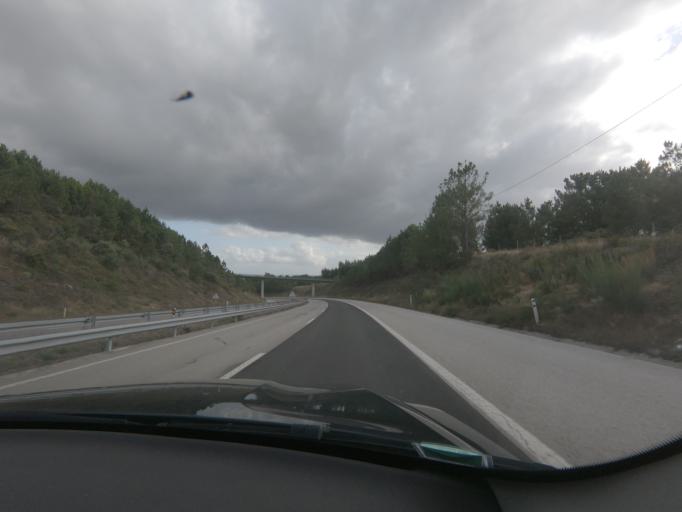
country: PT
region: Viseu
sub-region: Castro Daire
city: Castro Daire
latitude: 40.9264
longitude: -7.9171
